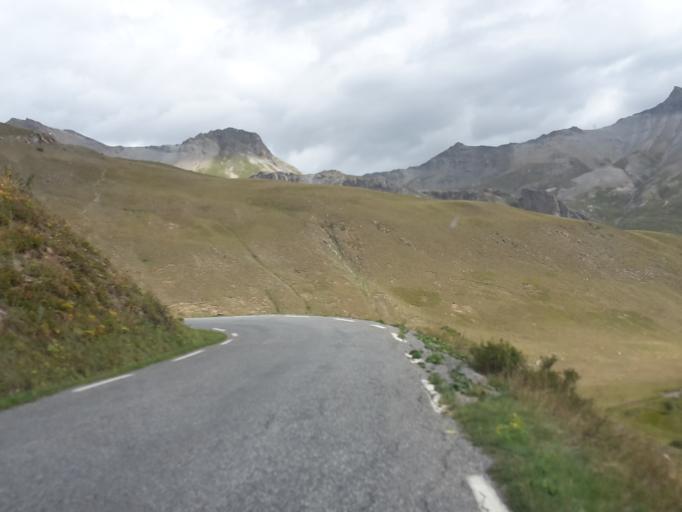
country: FR
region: Provence-Alpes-Cote d'Azur
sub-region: Departement des Hautes-Alpes
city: Le Monetier-les-Bains
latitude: 45.0378
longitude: 6.4028
